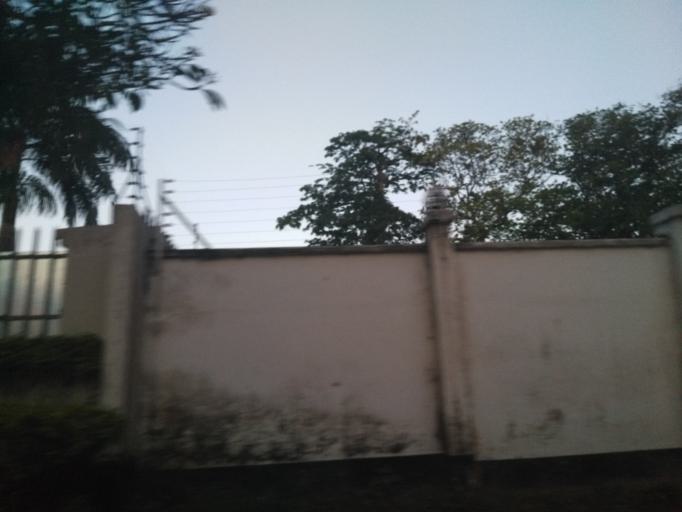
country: TZ
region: Dar es Salaam
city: Magomeni
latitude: -6.7689
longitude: 39.2781
